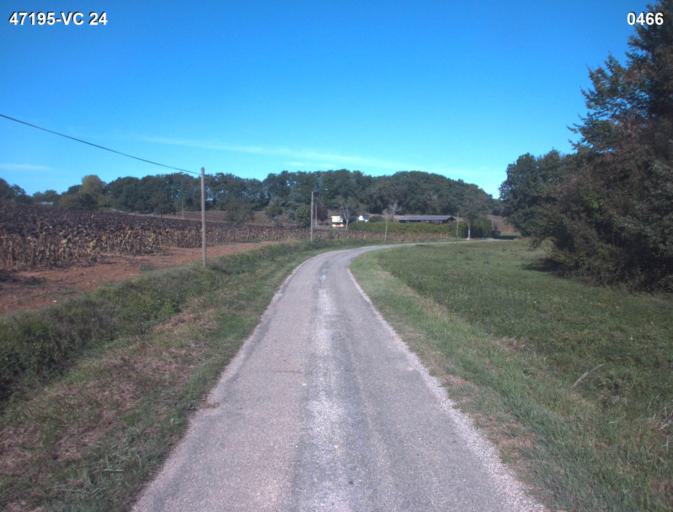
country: FR
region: Aquitaine
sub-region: Departement du Lot-et-Garonne
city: Nerac
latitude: 44.1657
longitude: 0.3636
